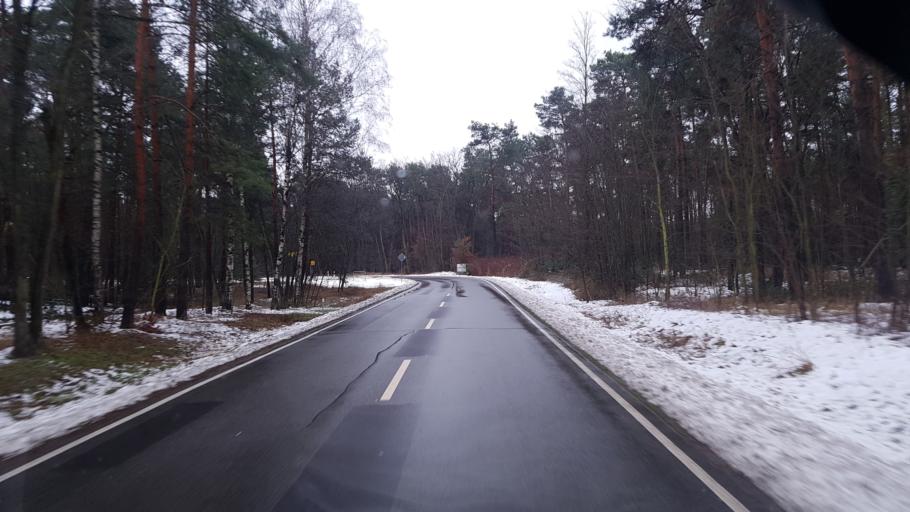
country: DE
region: Brandenburg
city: Schenkendobern
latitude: 51.9065
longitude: 14.6294
